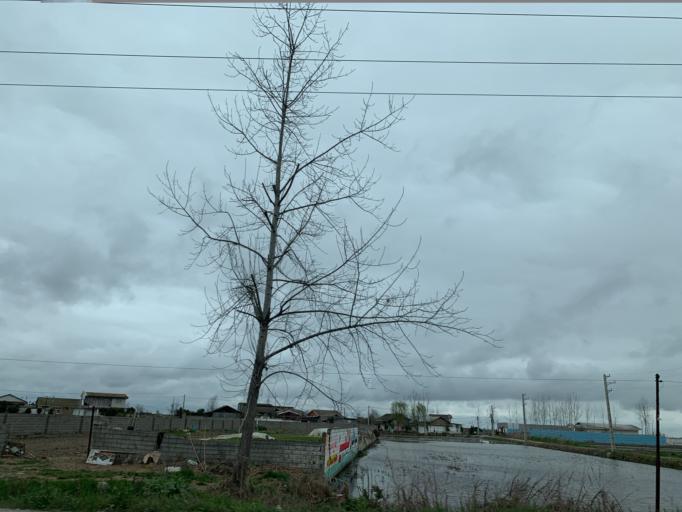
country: IR
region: Mazandaran
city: Babol
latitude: 36.5105
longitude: 52.5522
